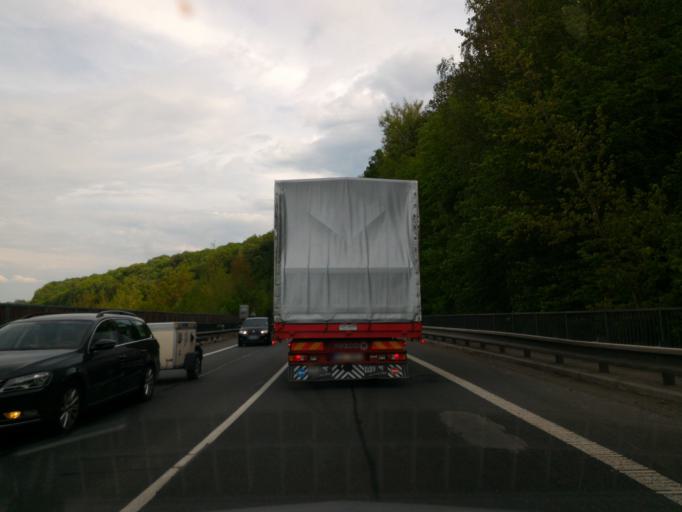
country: CZ
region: Central Bohemia
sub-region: Okres Mlada Boleslav
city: Mlada Boleslav
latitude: 50.4498
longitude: 14.8719
